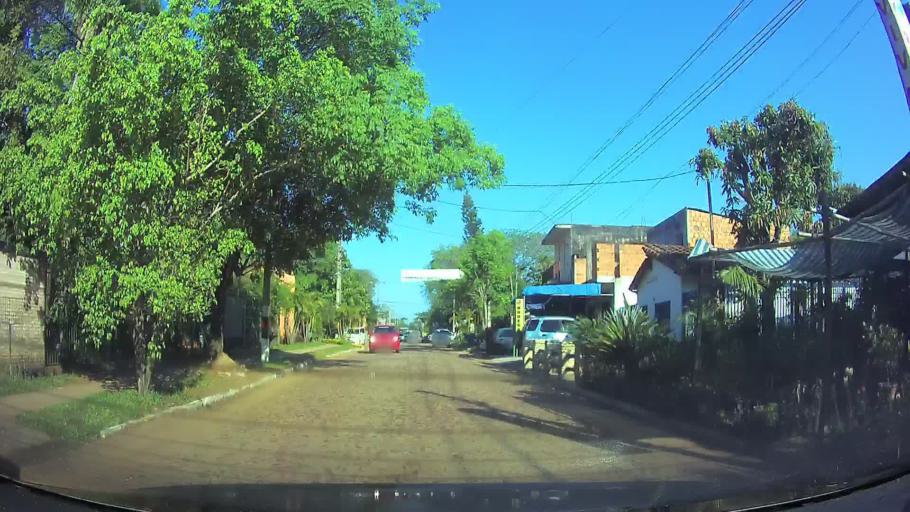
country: PY
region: Central
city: Aregua
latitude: -25.3080
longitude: -57.3841
